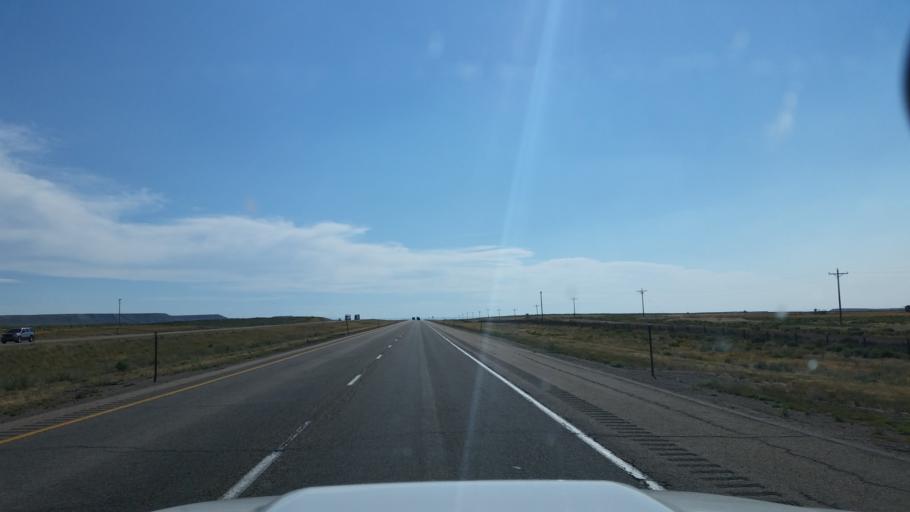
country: US
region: Wyoming
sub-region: Uinta County
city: Lyman
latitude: 41.4586
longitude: -110.0602
